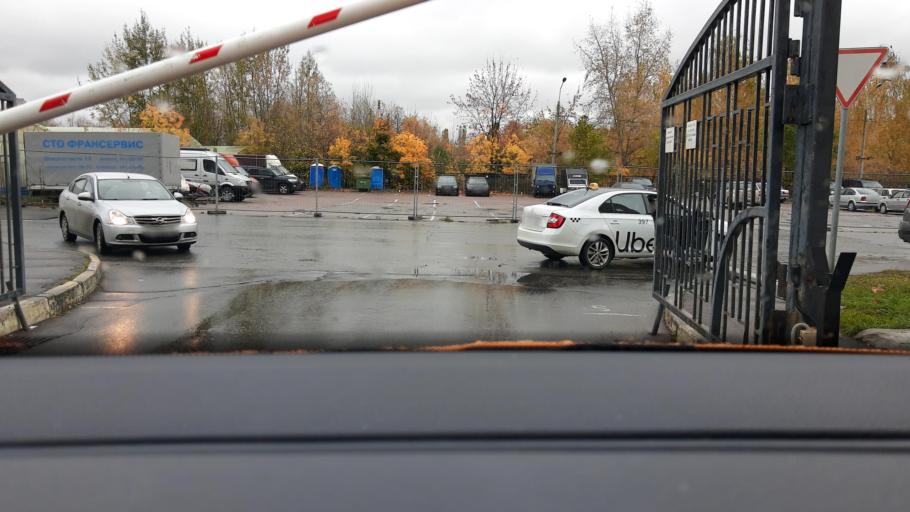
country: RU
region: Moscow
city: Strogino
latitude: 55.8032
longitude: 37.4140
